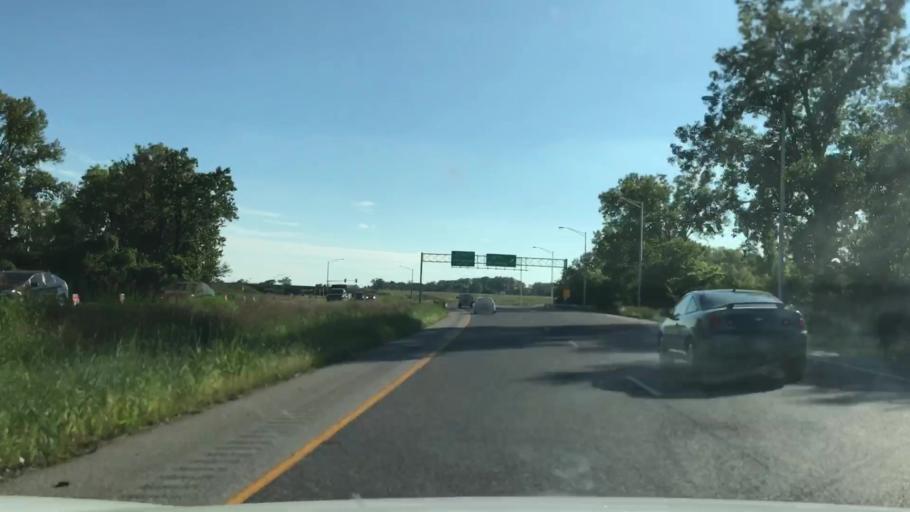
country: US
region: Illinois
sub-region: Madison County
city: Mitchell
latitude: 38.7706
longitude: -90.1216
